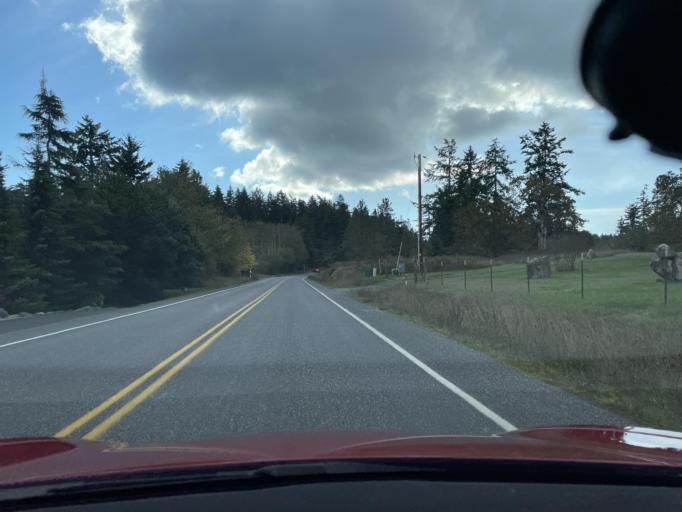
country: US
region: Washington
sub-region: San Juan County
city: Friday Harbor
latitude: 48.4988
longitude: -123.0336
